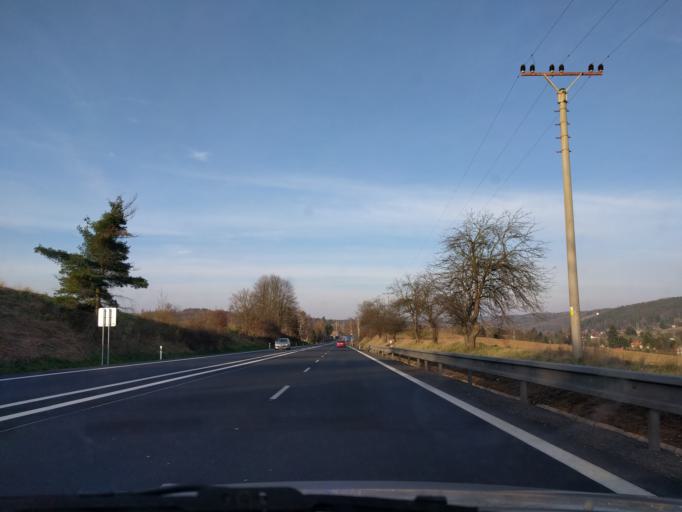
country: CZ
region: Central Bohemia
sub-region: Okres Benesov
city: Cercany
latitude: 49.8576
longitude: 14.6919
